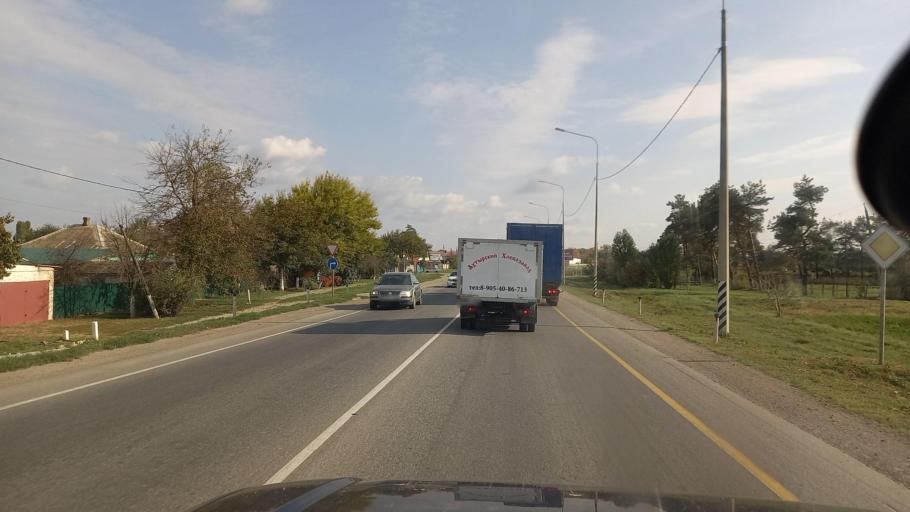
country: RU
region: Krasnodarskiy
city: Krymsk
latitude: 44.9111
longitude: 38.0103
